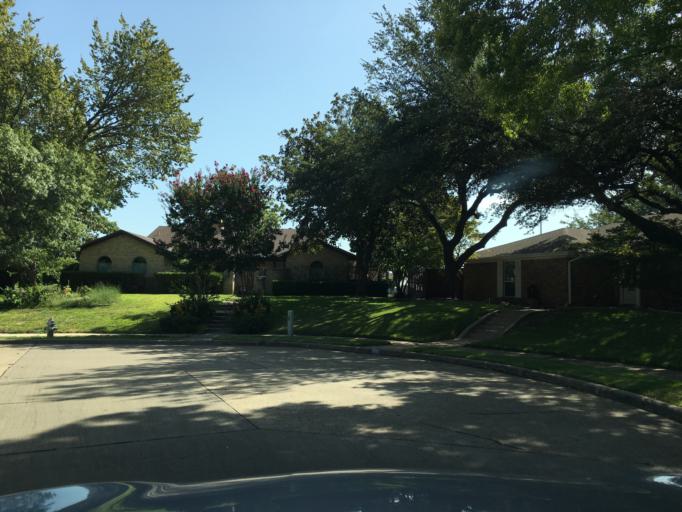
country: US
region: Texas
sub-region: Dallas County
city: Garland
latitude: 32.8731
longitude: -96.6224
